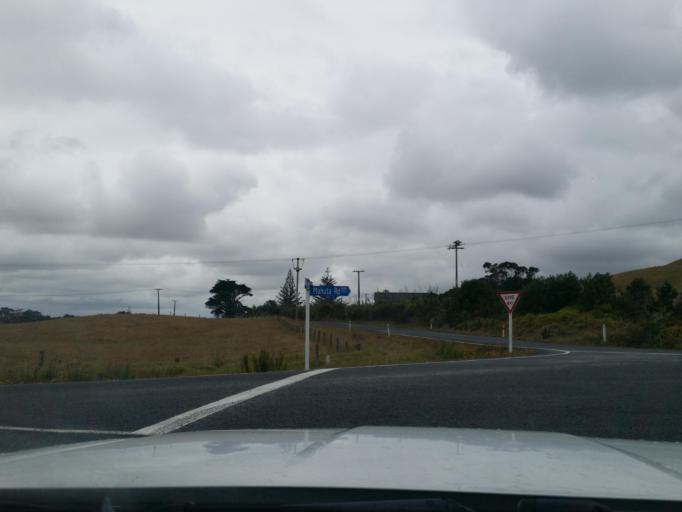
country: NZ
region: Northland
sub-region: Kaipara District
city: Dargaville
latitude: -35.9982
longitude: 173.8002
